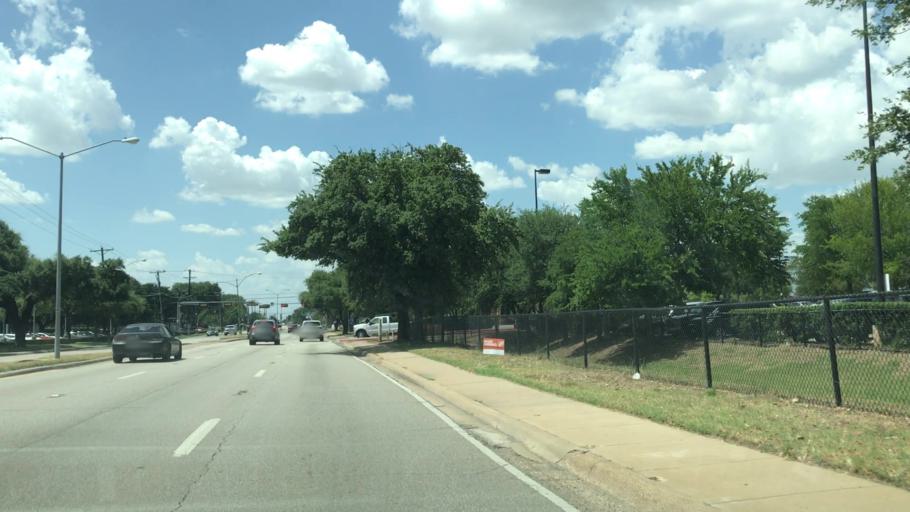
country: US
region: Texas
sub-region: Dallas County
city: University Park
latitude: 32.8325
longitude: -96.8285
